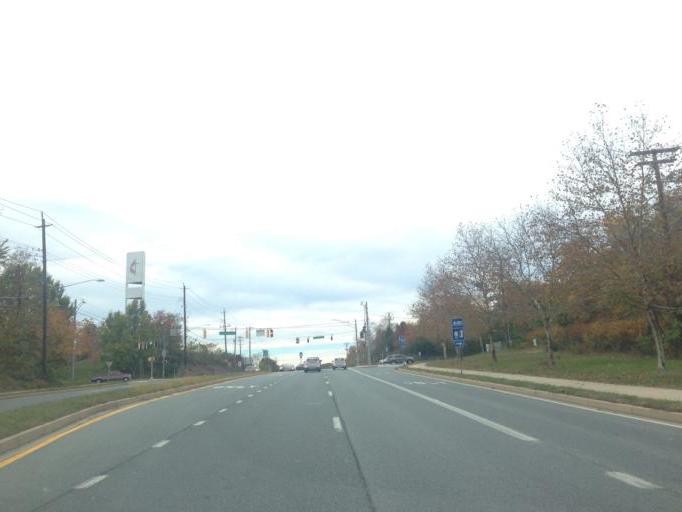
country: US
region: Maryland
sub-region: Montgomery County
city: Germantown
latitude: 39.1623
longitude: -77.2818
